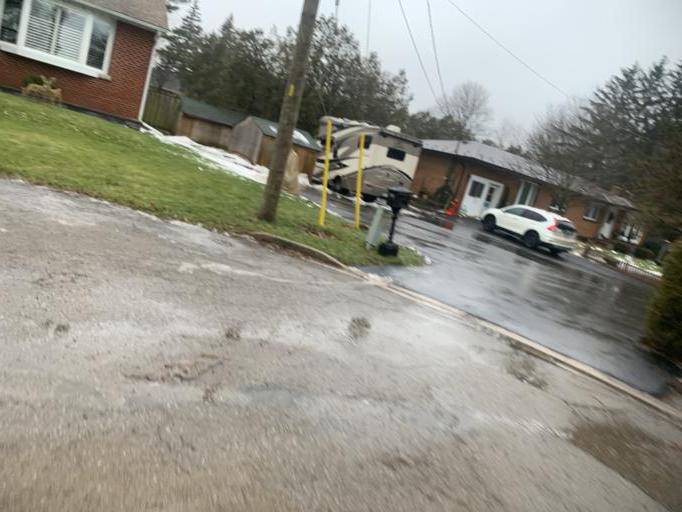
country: CA
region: Ontario
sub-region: Halton
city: Milton
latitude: 43.6563
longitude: -79.9335
